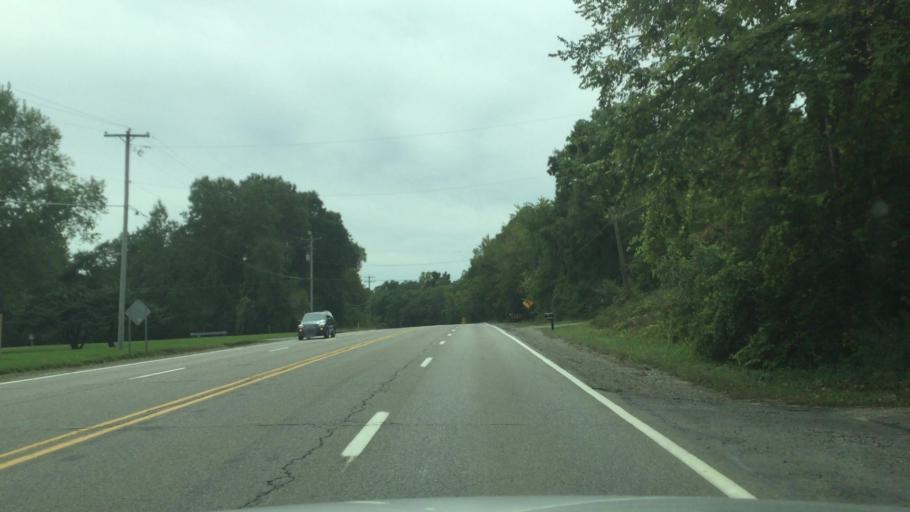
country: US
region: Michigan
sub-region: Oakland County
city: Holly
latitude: 42.8061
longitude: -83.5354
